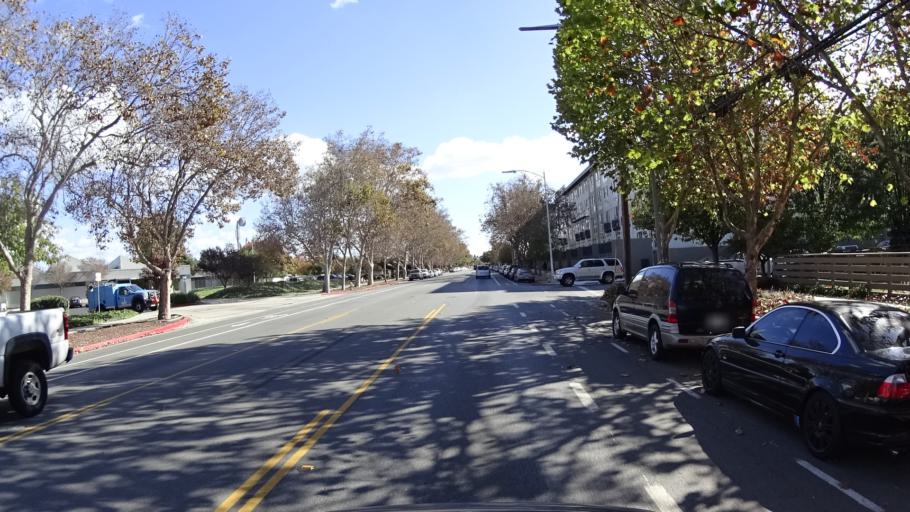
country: US
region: California
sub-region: Santa Clara County
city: San Jose
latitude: 37.3358
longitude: -121.9081
